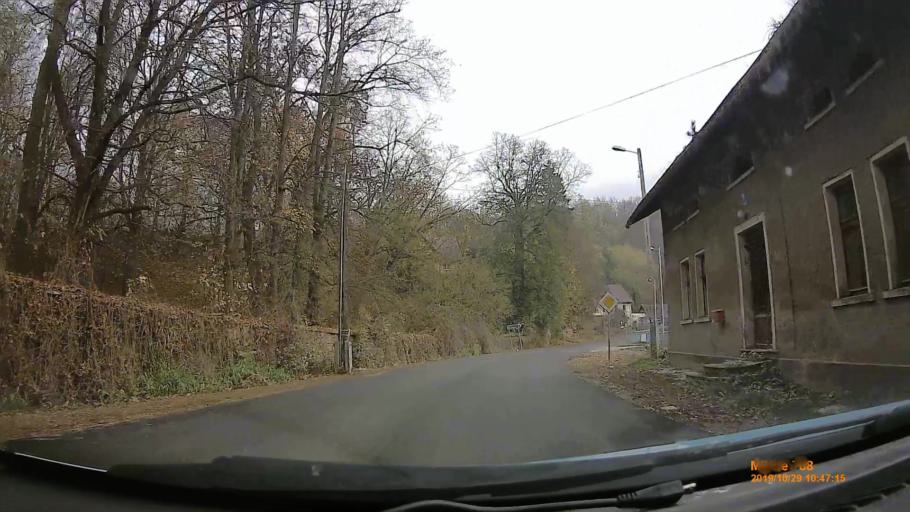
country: PL
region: Lower Silesian Voivodeship
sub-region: Powiat klodzki
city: Radkow
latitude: 50.5544
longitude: 16.4315
